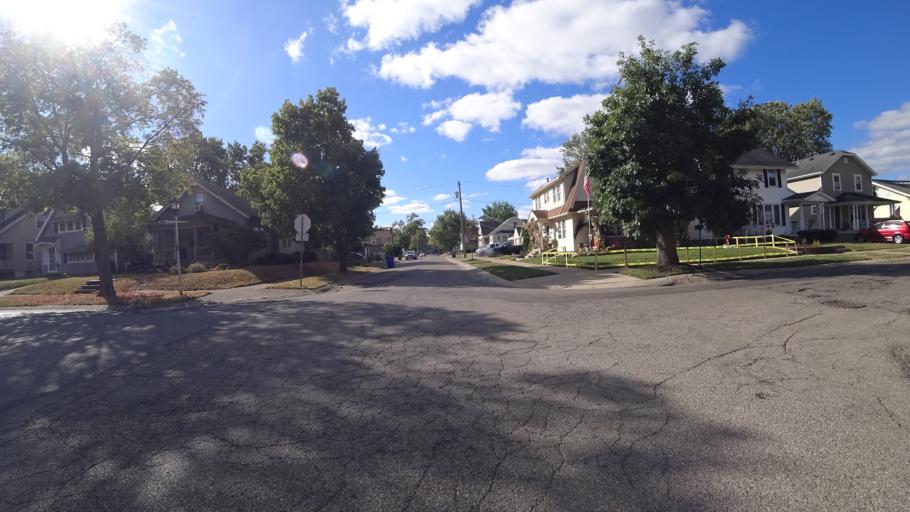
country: US
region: Ohio
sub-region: Butler County
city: Fairfield
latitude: 39.3661
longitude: -84.5511
